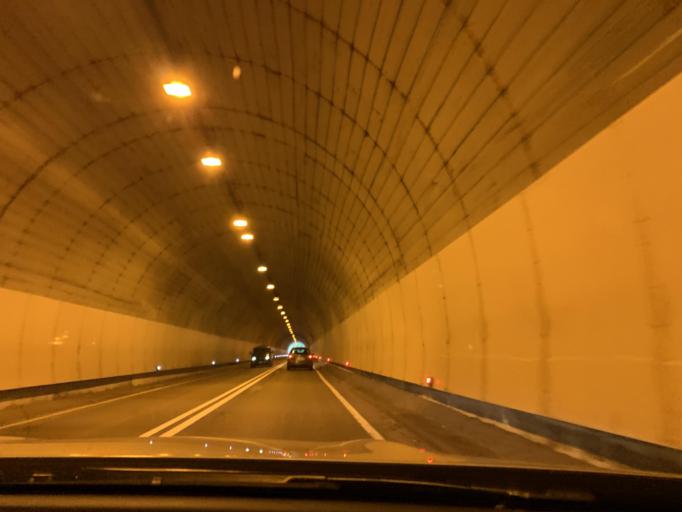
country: IT
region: Trentino-Alto Adige
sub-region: Bolzano
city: Nova Levante
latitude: 46.4257
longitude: 11.4989
